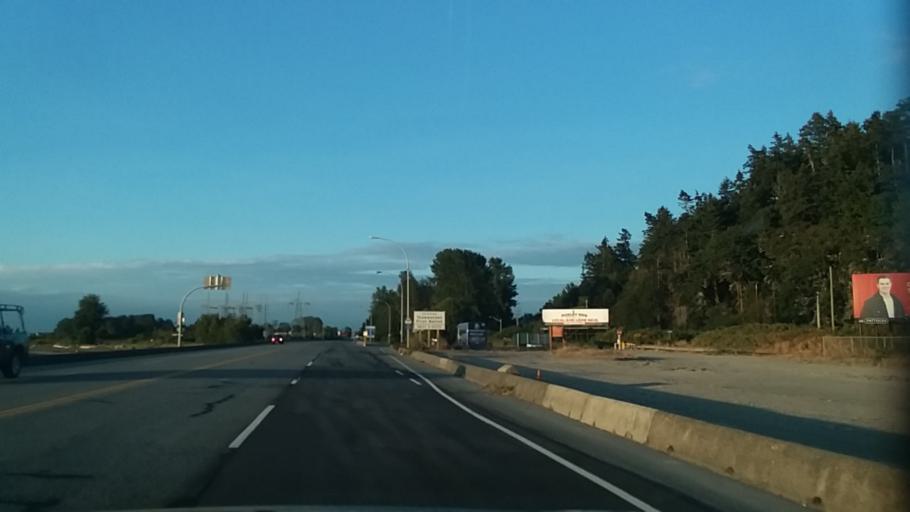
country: US
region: Washington
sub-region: Whatcom County
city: Point Roberts
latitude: 49.0254
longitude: -123.1031
